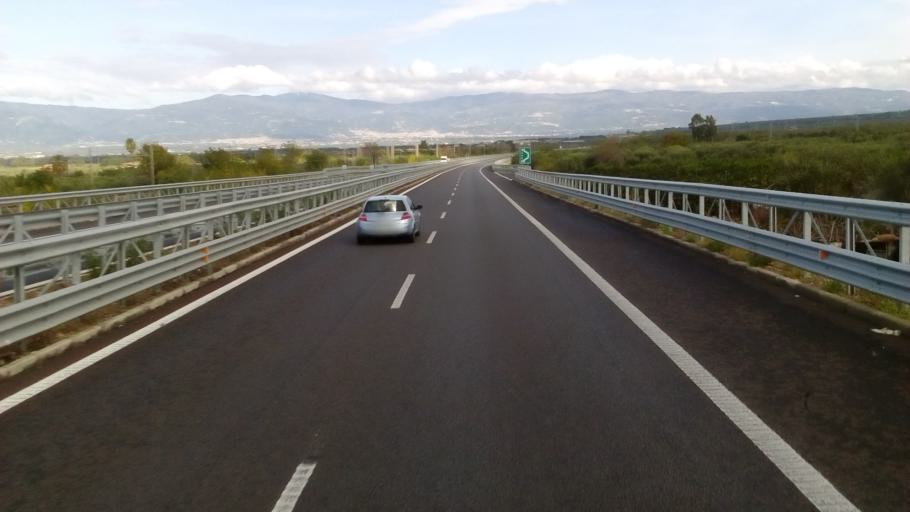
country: IT
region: Calabria
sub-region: Provincia di Catanzaro
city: Acconia
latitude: 38.8418
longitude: 16.2631
